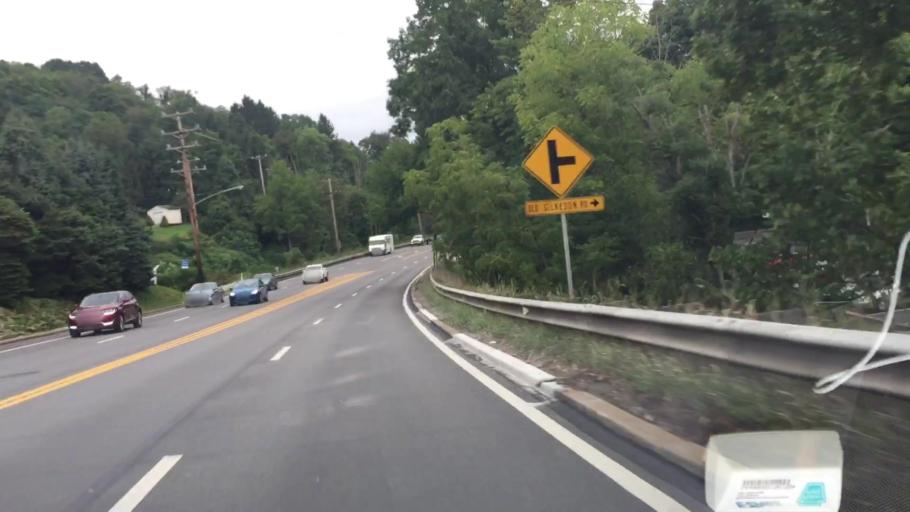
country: US
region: Pennsylvania
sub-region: Allegheny County
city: Mount Lebanon
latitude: 40.3587
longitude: -80.0590
